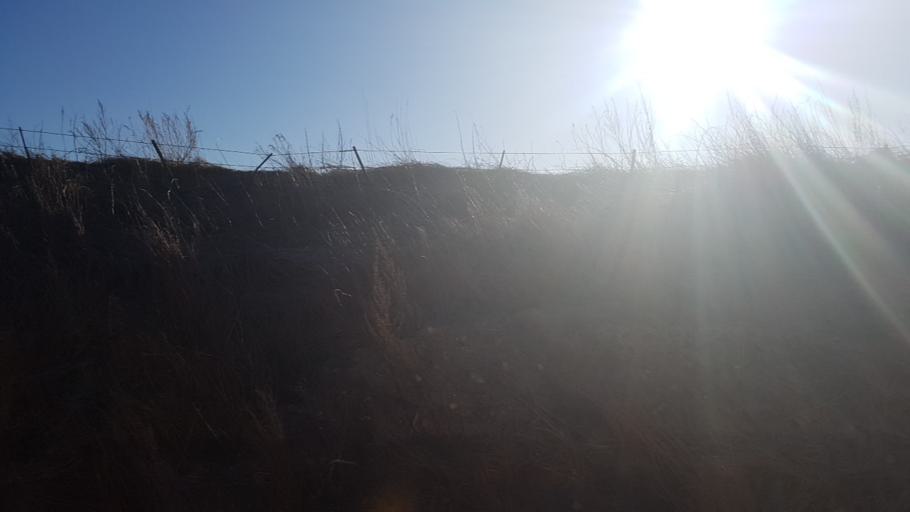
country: NO
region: Nord-Trondelag
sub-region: Levanger
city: Levanger
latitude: 63.7308
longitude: 11.2856
